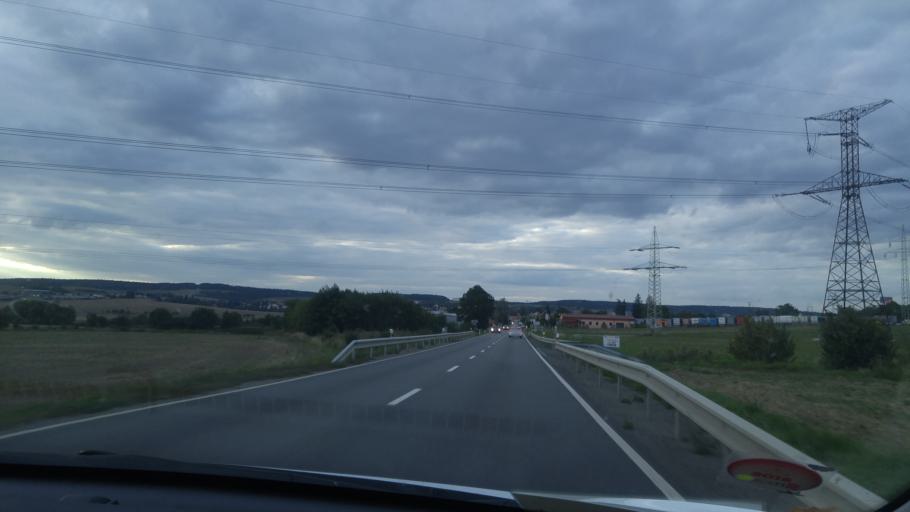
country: CZ
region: South Moravian
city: Ricany
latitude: 49.2029
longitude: 16.4193
